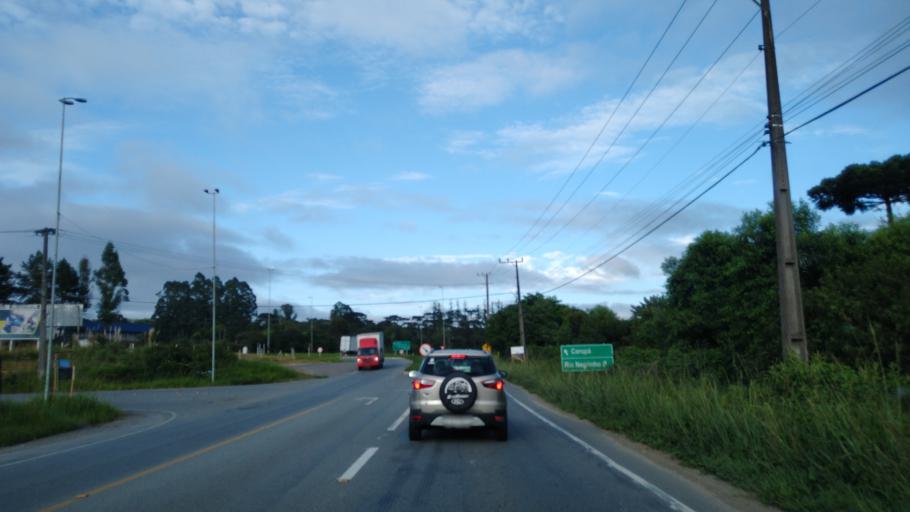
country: BR
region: Santa Catarina
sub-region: Rio Negrinho
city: Rio Negrinho
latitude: -26.2448
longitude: -49.4593
